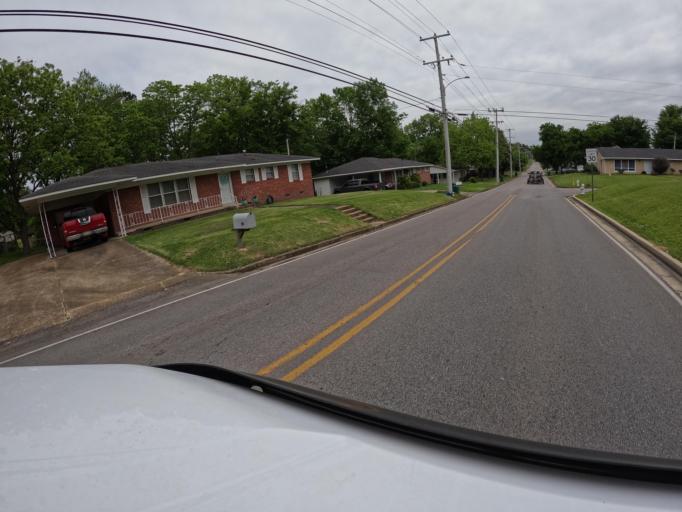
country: US
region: Mississippi
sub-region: Lee County
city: Tupelo
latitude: 34.2657
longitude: -88.7377
